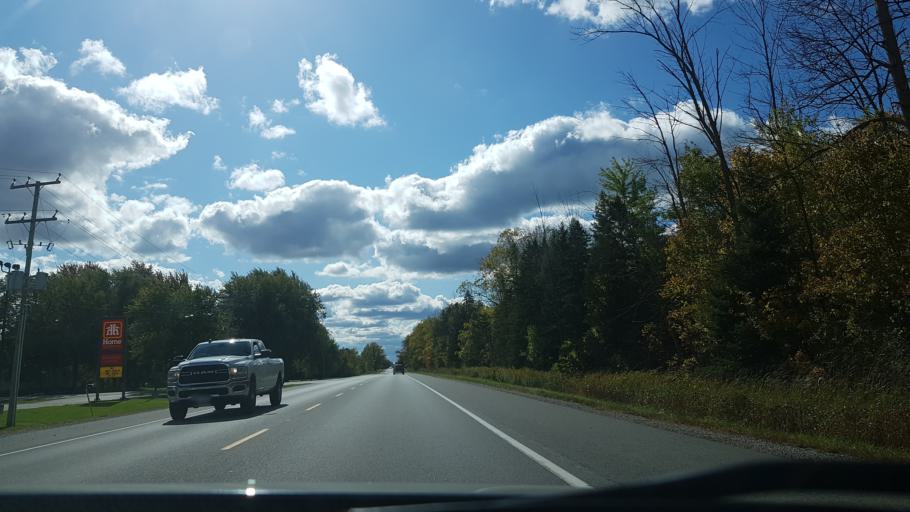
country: CA
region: Ontario
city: Bluewater
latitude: 43.3279
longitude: -81.7441
